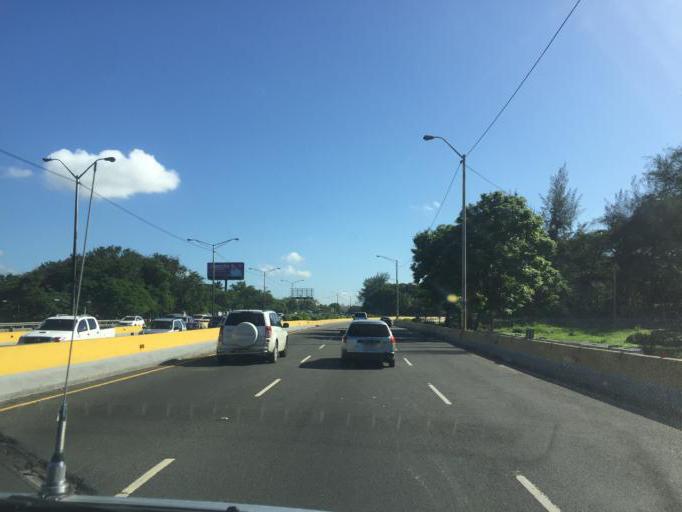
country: DO
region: Santo Domingo
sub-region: Santo Domingo
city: Santo Domingo Este
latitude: 18.4847
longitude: -69.8540
